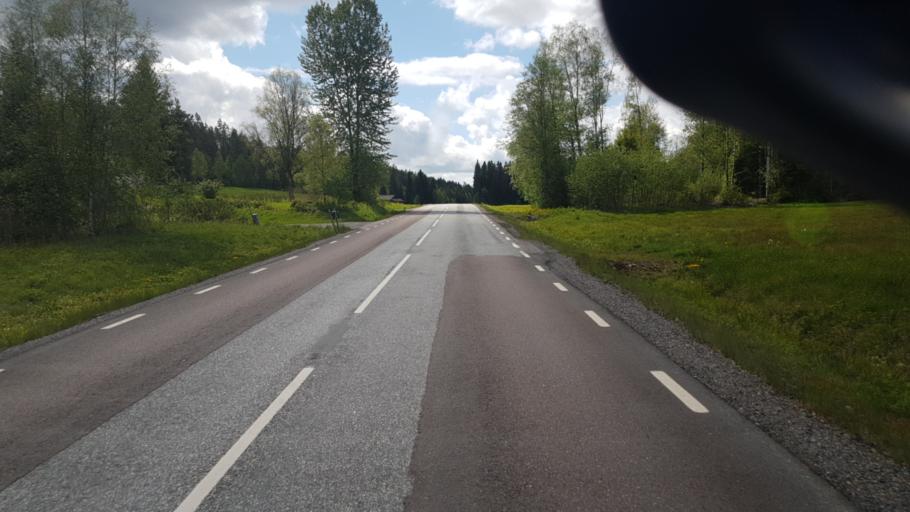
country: SE
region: Vaermland
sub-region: Arjangs Kommun
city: Arjaeng
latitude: 59.5731
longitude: 12.1237
